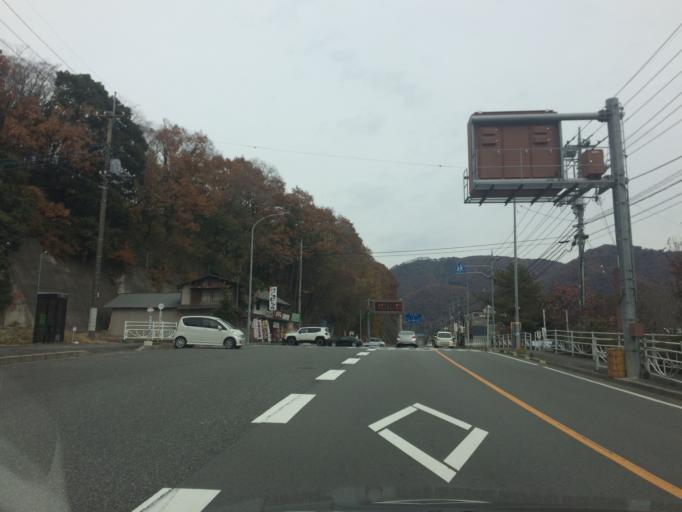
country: JP
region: Yamanashi
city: Ryuo
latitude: 35.4162
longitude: 138.4431
